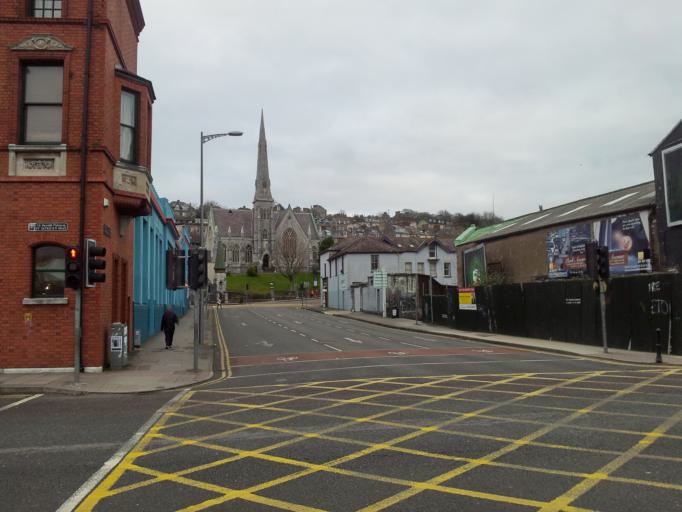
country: IE
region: Munster
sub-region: County Cork
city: Cork
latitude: 51.9005
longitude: -8.4657
